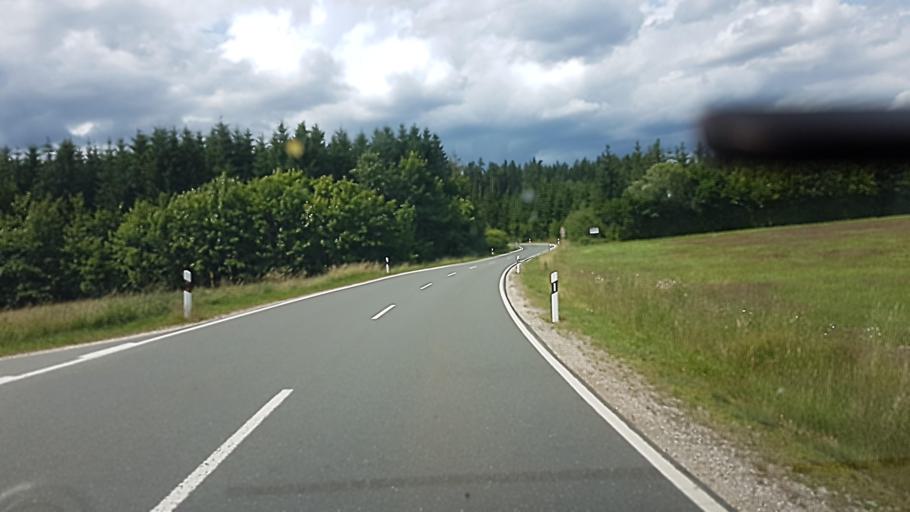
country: DE
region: Bavaria
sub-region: Upper Palatinate
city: Brand
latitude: 49.9613
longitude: 11.8969
